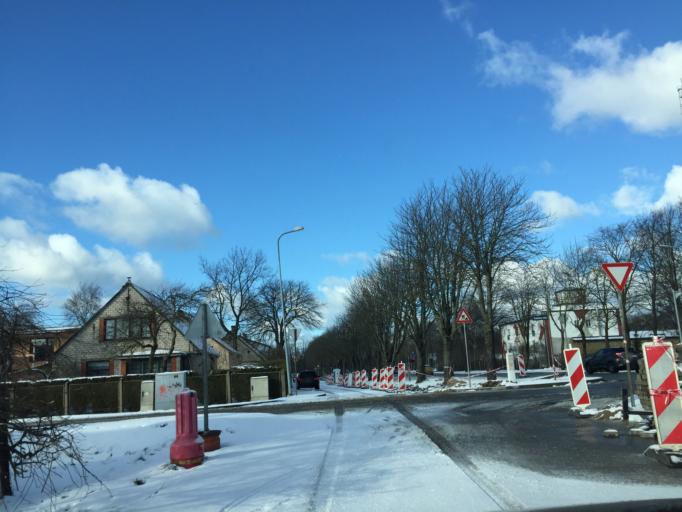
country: LV
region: Ventspils
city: Ventspils
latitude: 57.3806
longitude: 21.5662
